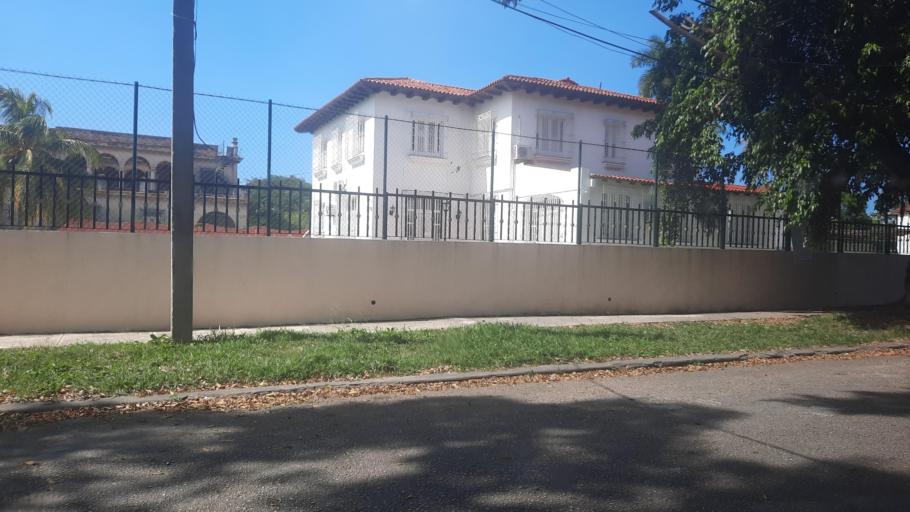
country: CU
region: La Habana
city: Havana
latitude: 23.1200
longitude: -82.4133
